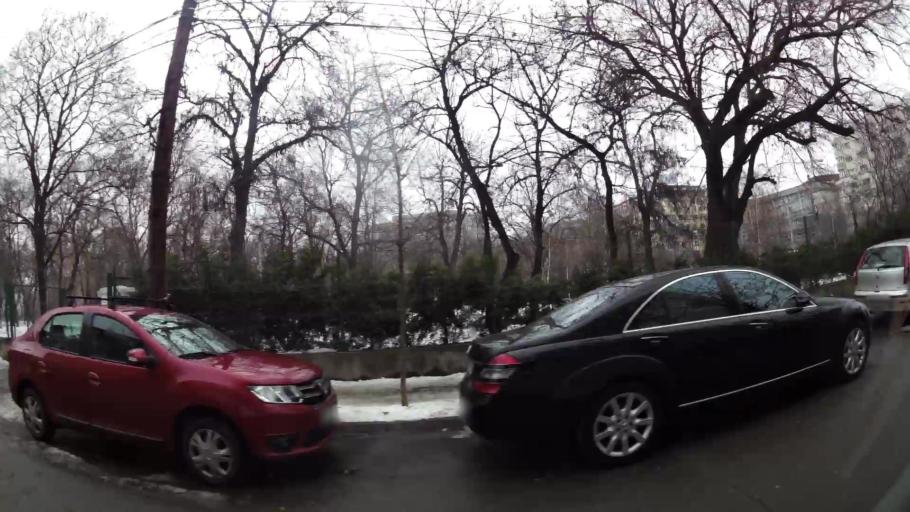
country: RO
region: Bucuresti
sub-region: Municipiul Bucuresti
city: Bucuresti
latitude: 44.4572
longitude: 26.0654
